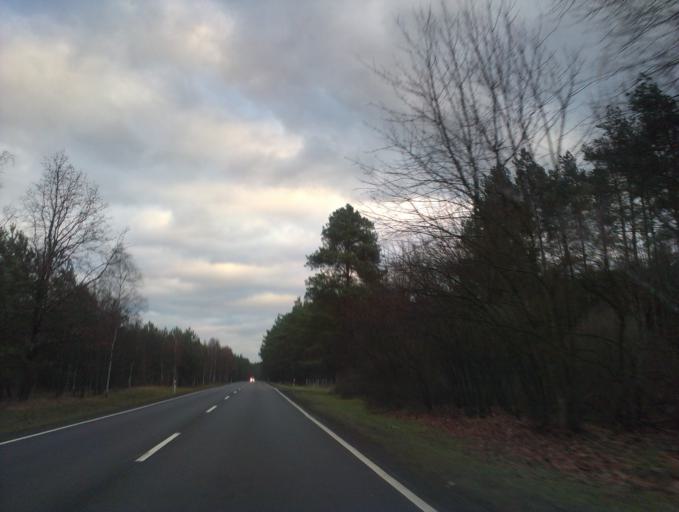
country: PL
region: Greater Poland Voivodeship
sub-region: Powiat pilski
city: Pila
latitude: 53.1912
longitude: 16.7672
